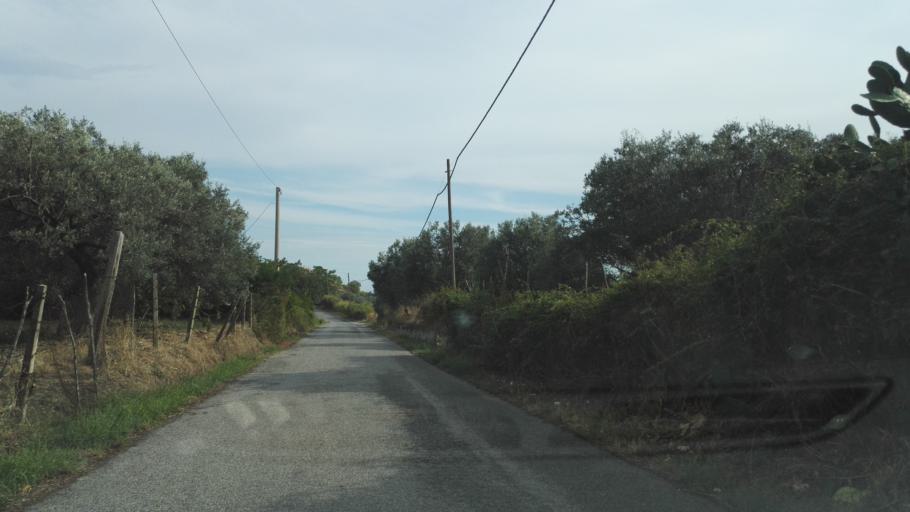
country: IT
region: Calabria
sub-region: Provincia di Reggio Calabria
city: Stignano
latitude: 38.4246
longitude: 16.4649
